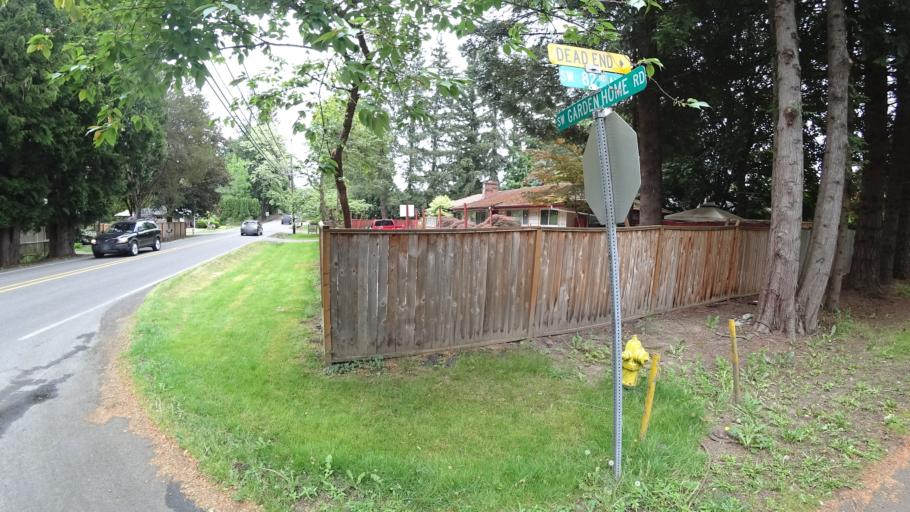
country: US
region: Oregon
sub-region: Washington County
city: Garden Home-Whitford
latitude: 45.4657
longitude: -122.7611
